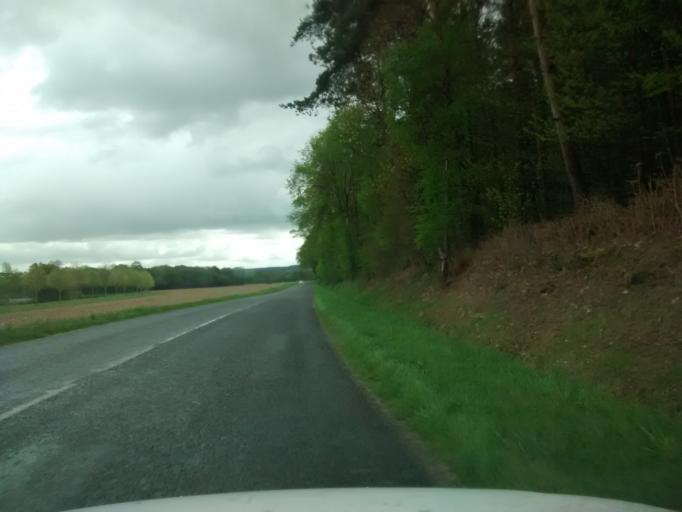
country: FR
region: Brittany
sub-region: Departement du Morbihan
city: Malestroit
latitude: 47.8036
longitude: -2.3399
